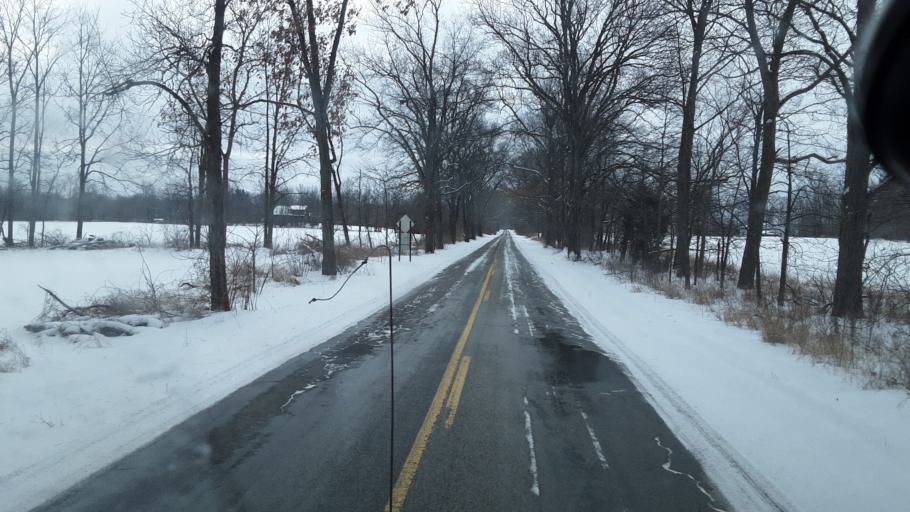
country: US
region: Michigan
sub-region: Ingham County
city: Leslie
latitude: 42.5082
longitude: -84.3892
